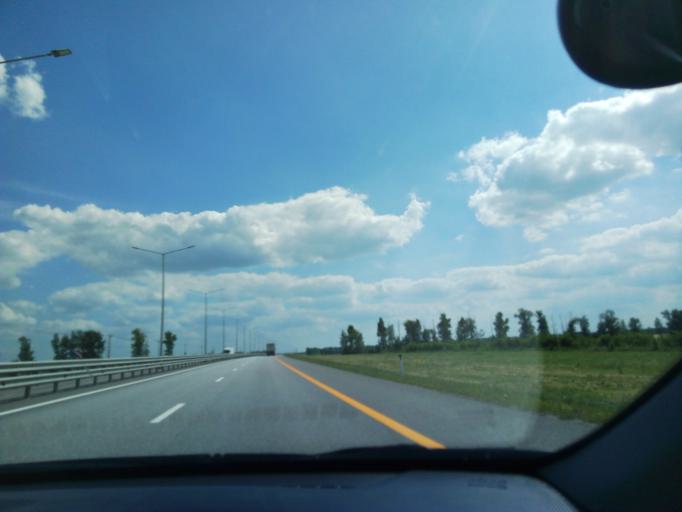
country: RU
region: Voronezj
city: Podkletnoye
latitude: 51.5265
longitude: 39.5101
